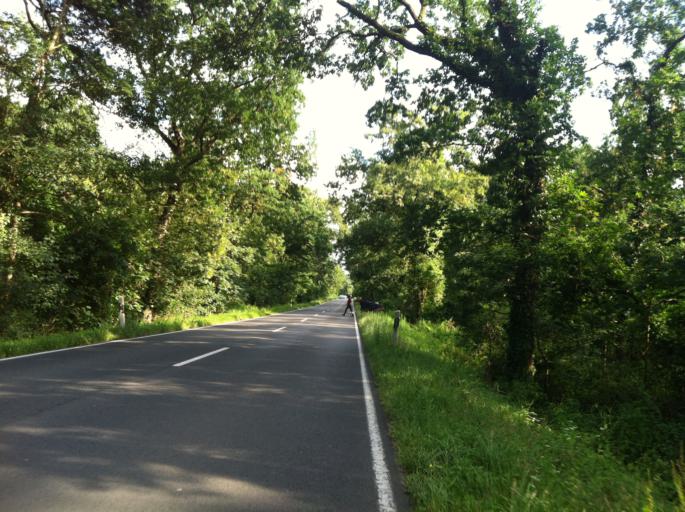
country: DE
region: Rheinland-Pfalz
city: Budenheim
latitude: 50.0129
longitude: 8.1687
